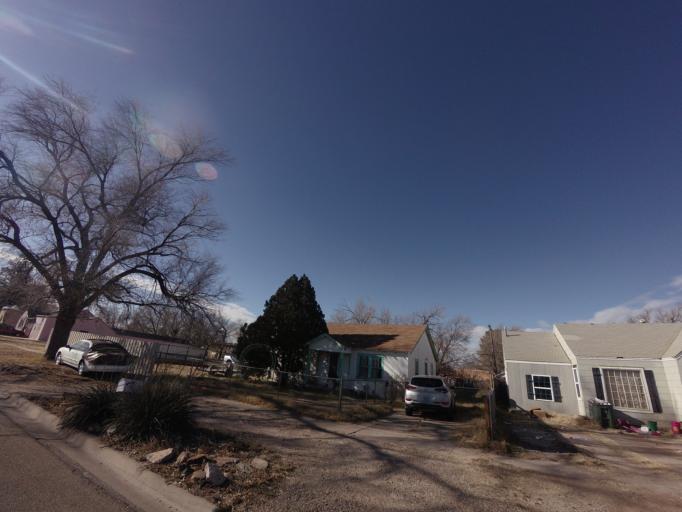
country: US
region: New Mexico
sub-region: Curry County
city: Clovis
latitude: 34.4092
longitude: -103.2142
